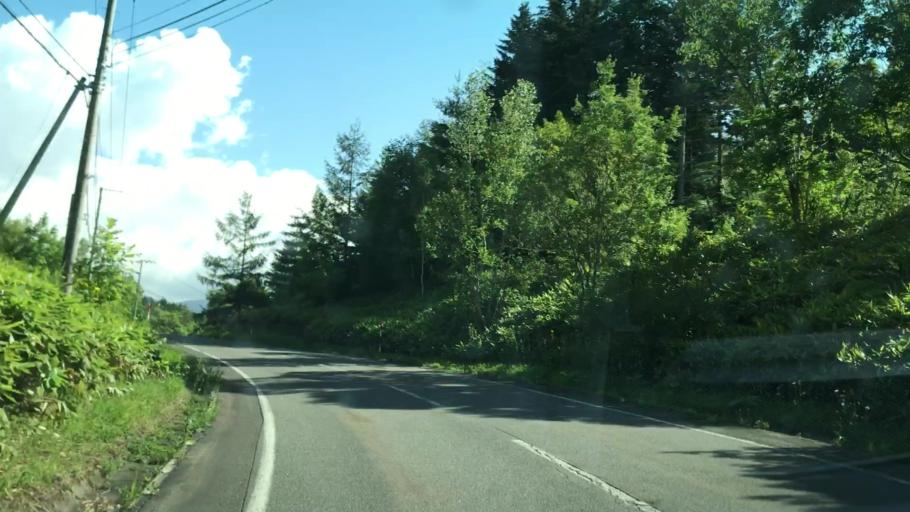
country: JP
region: Hokkaido
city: Shimo-furano
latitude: 42.8609
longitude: 142.4403
